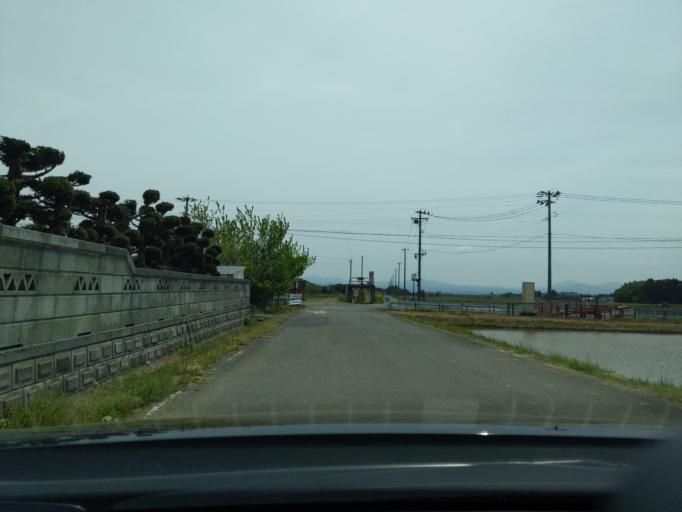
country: JP
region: Fukushima
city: Koriyama
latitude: 37.3967
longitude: 140.2882
